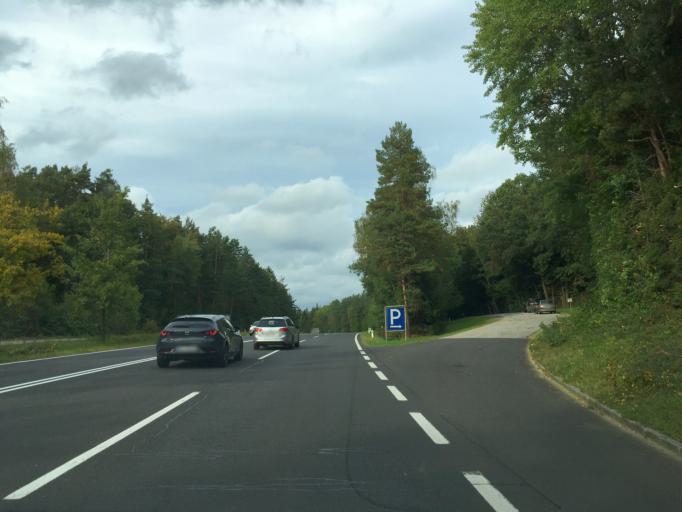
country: AT
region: Styria
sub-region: Politischer Bezirk Hartberg-Fuerstenfeld
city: Grafendorf bei Hartberg
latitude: 47.3509
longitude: 16.0105
